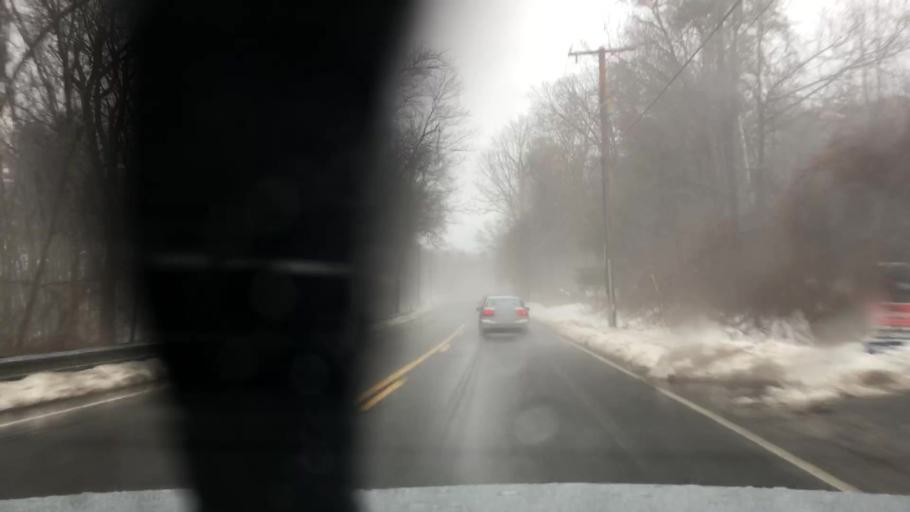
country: US
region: Massachusetts
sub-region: Hampshire County
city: Granby
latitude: 42.2434
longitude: -72.4797
